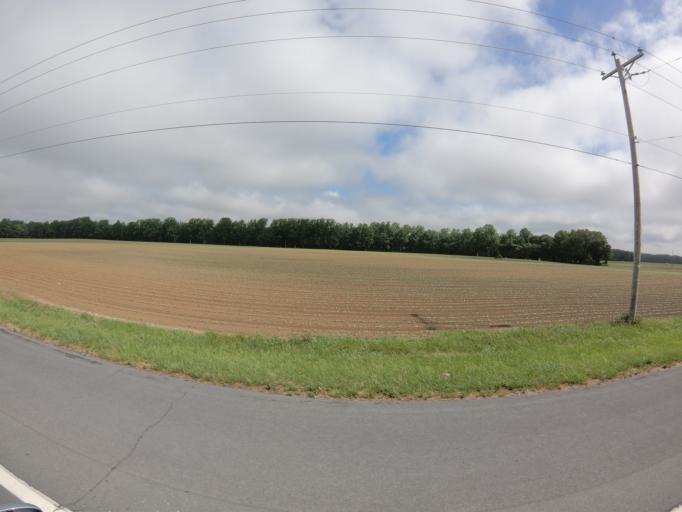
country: US
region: Delaware
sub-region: Kent County
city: Riverview
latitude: 39.0060
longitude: -75.5298
